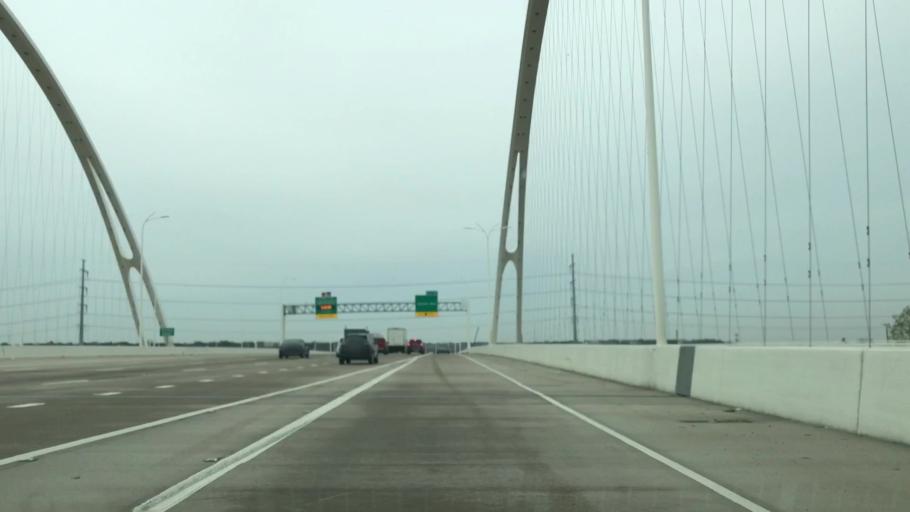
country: US
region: Texas
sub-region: Dallas County
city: Dallas
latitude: 32.7709
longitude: -96.8166
